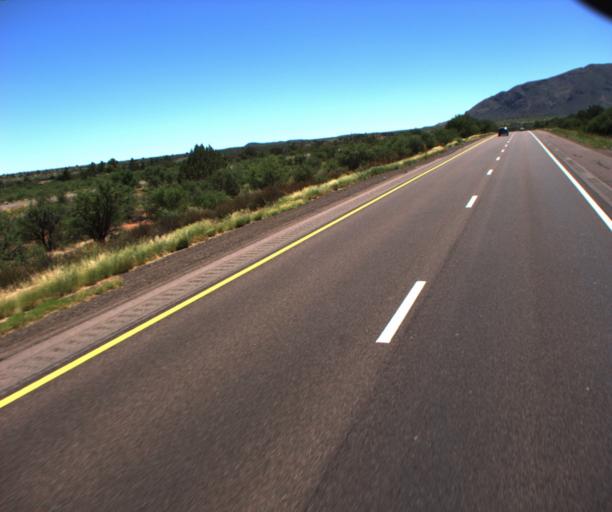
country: US
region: Arizona
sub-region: Gila County
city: Payson
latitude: 34.0673
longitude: -111.3599
